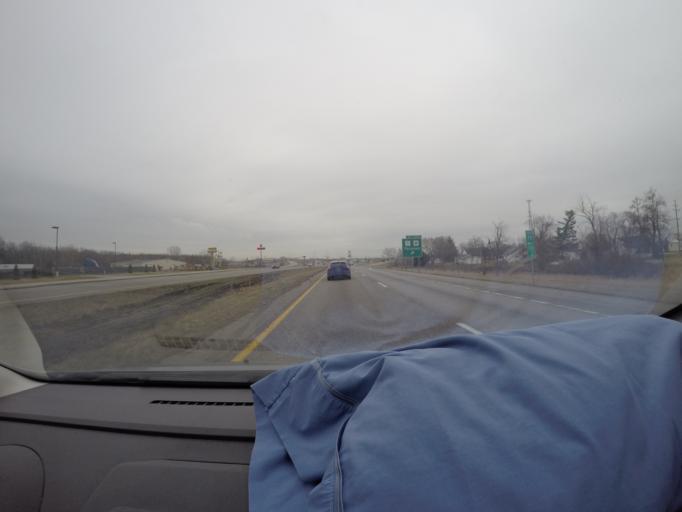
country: US
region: Missouri
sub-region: Warren County
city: Wright City
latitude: 38.8173
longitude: -90.9590
